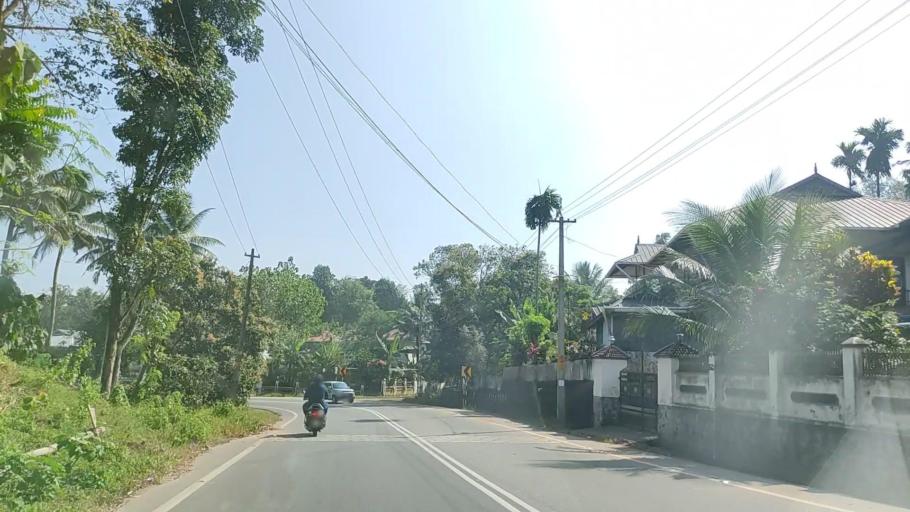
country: IN
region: Kerala
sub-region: Kollam
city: Punalur
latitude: 8.9349
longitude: 76.9515
